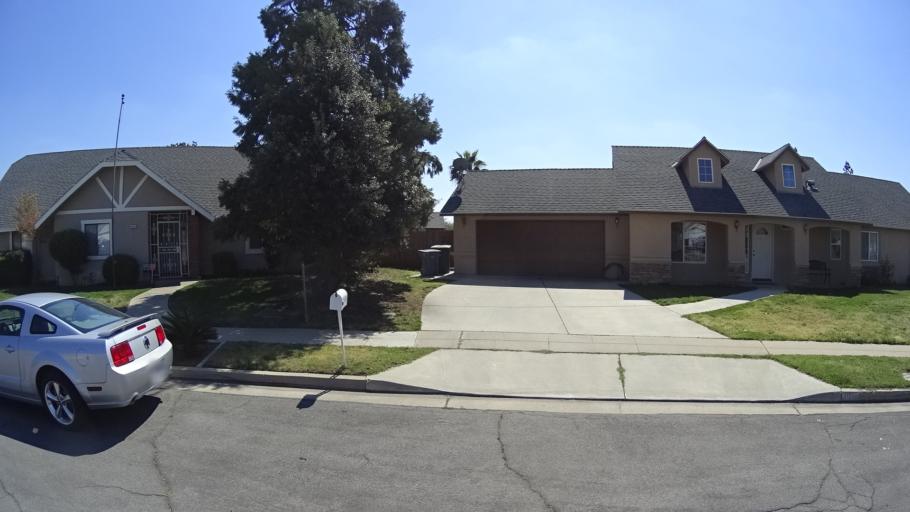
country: US
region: California
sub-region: Fresno County
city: Tarpey Village
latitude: 36.7991
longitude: -119.7345
